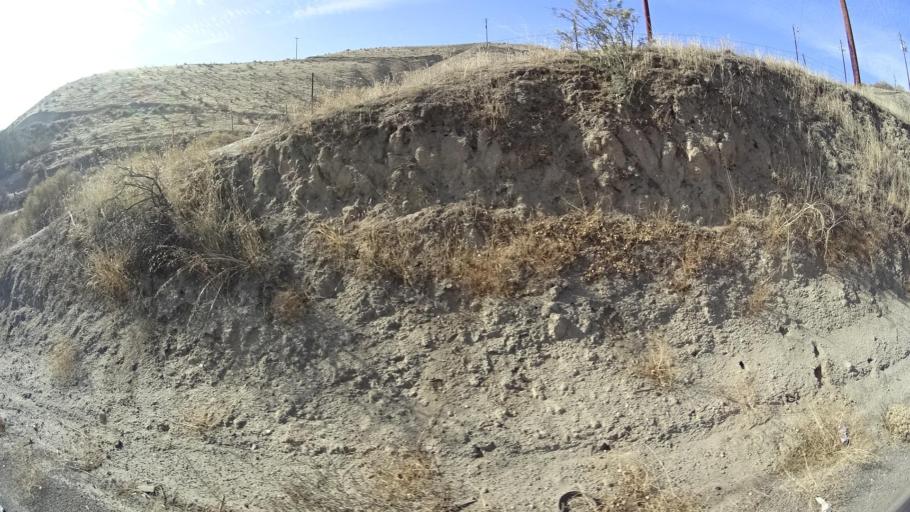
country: US
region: California
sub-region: Kern County
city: Oildale
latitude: 35.5556
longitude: -118.9587
